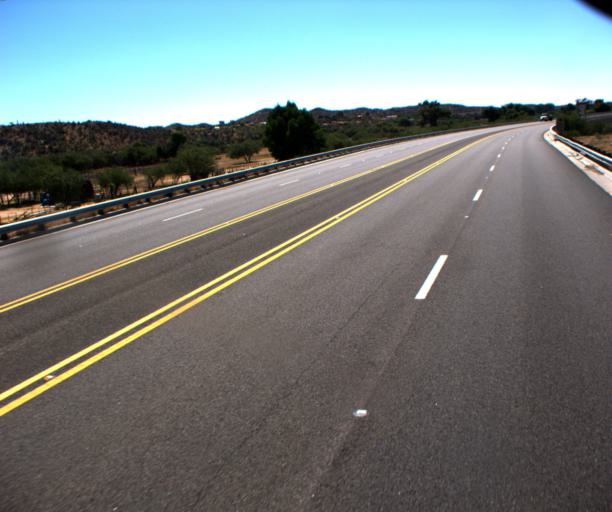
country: US
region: Arizona
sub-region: Maricopa County
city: Wickenburg
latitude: 33.9822
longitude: -112.7361
